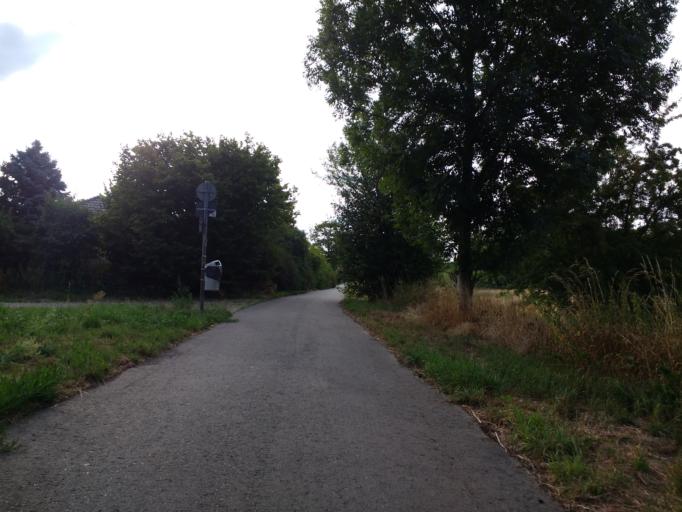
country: DE
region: Lower Saxony
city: Weyhausen
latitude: 52.4185
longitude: 10.6968
